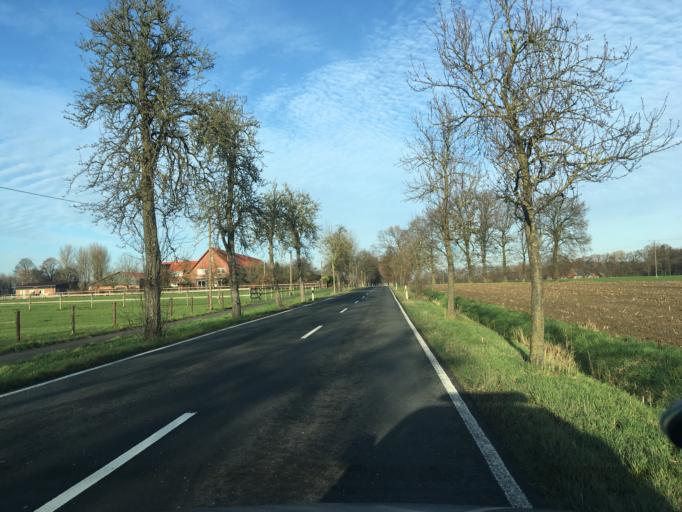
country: DE
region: North Rhine-Westphalia
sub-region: Regierungsbezirk Munster
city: Gescher
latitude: 51.9602
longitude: 7.0603
